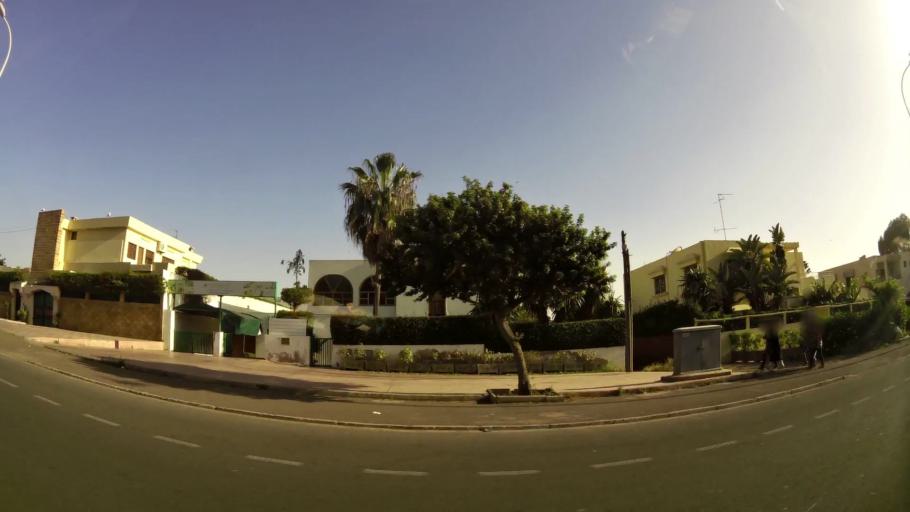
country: MA
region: Souss-Massa-Draa
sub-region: Agadir-Ida-ou-Tnan
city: Agadir
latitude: 30.4269
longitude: -9.5900
